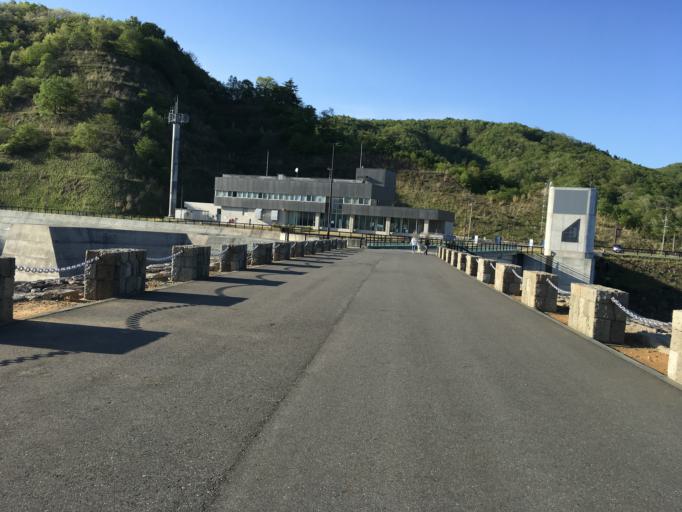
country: JP
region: Iwate
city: Mizusawa
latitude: 39.1239
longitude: 140.9199
